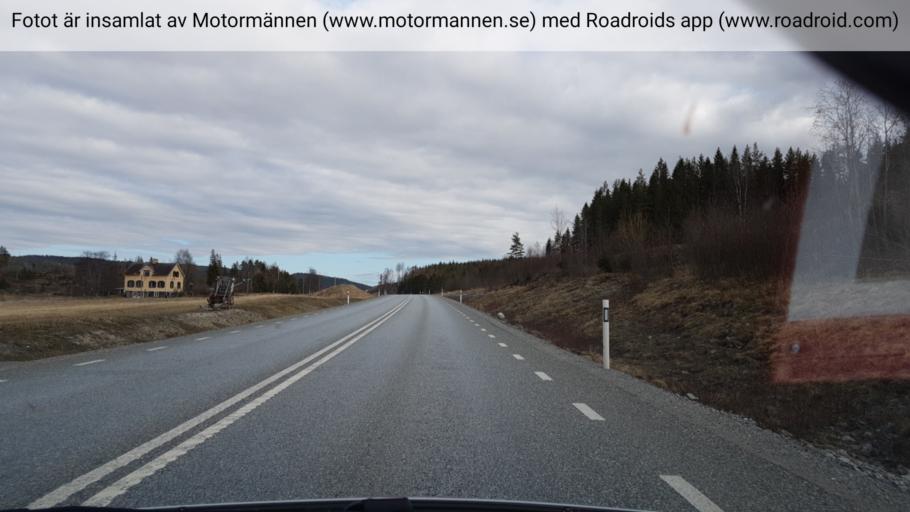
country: SE
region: Vaesternorrland
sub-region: Kramfors Kommun
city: Bollstabruk
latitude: 63.0383
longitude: 17.6508
